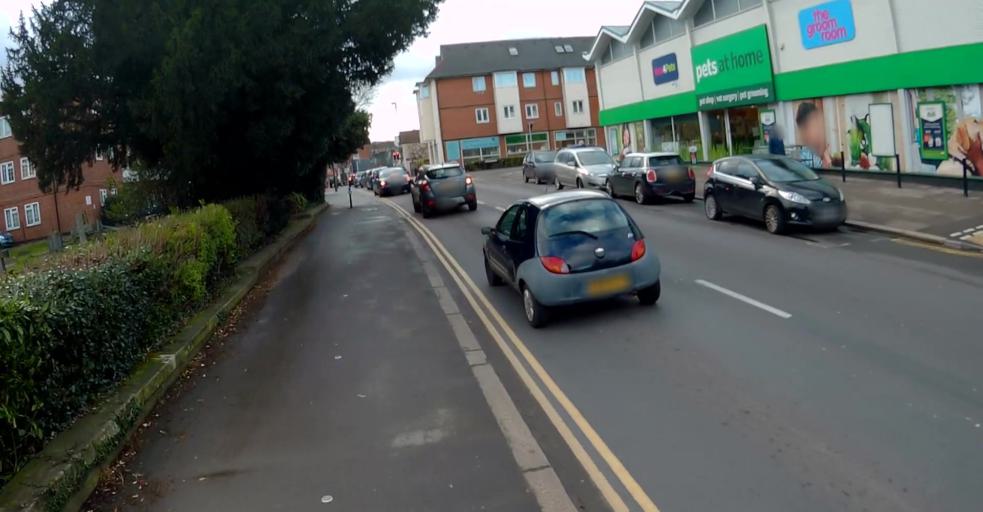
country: GB
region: England
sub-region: Surrey
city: Walton-on-Thames
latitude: 51.3880
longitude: -0.4175
